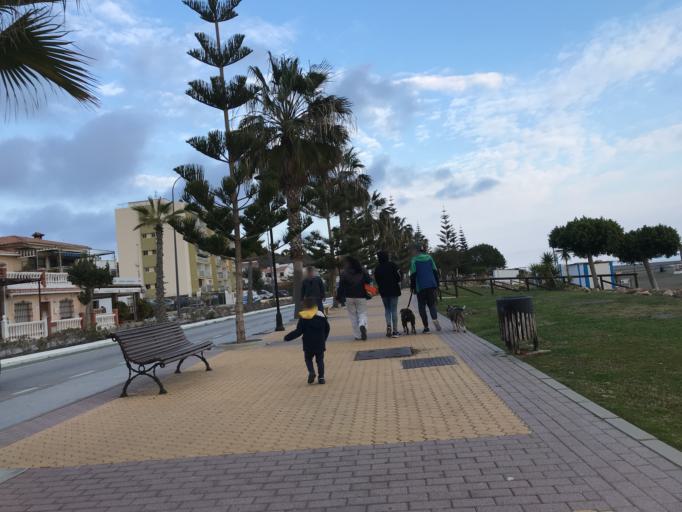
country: ES
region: Andalusia
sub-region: Provincia de Malaga
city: Valdes
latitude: 36.7161
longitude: -4.1922
